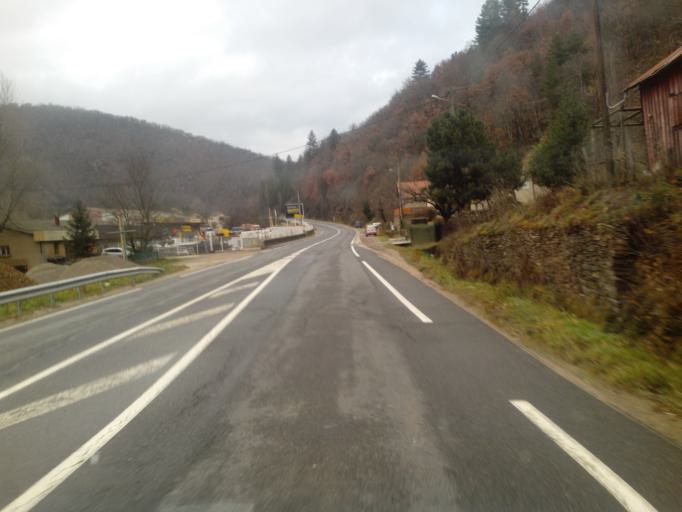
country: FR
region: Languedoc-Roussillon
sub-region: Departement de la Lozere
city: Florac
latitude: 44.3444
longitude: 3.5818
